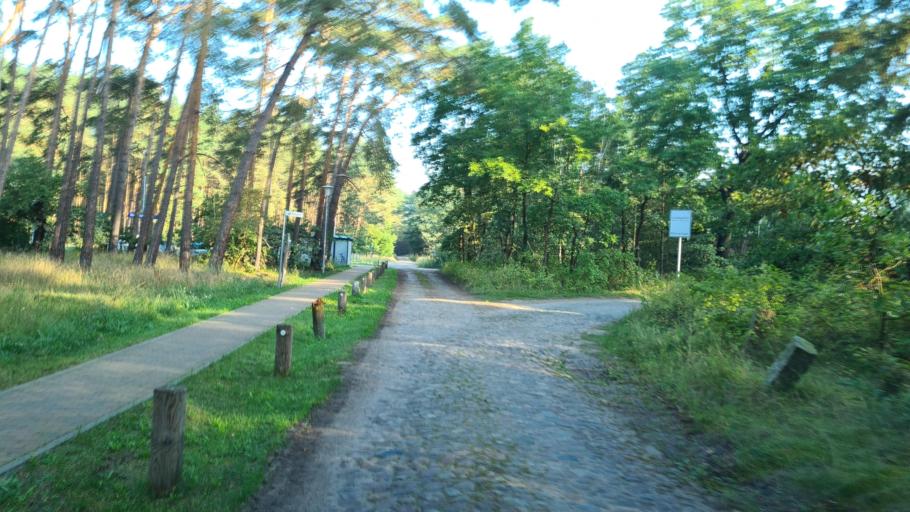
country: DE
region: Brandenburg
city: Treuenbrietzen
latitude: 52.1653
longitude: 12.9212
